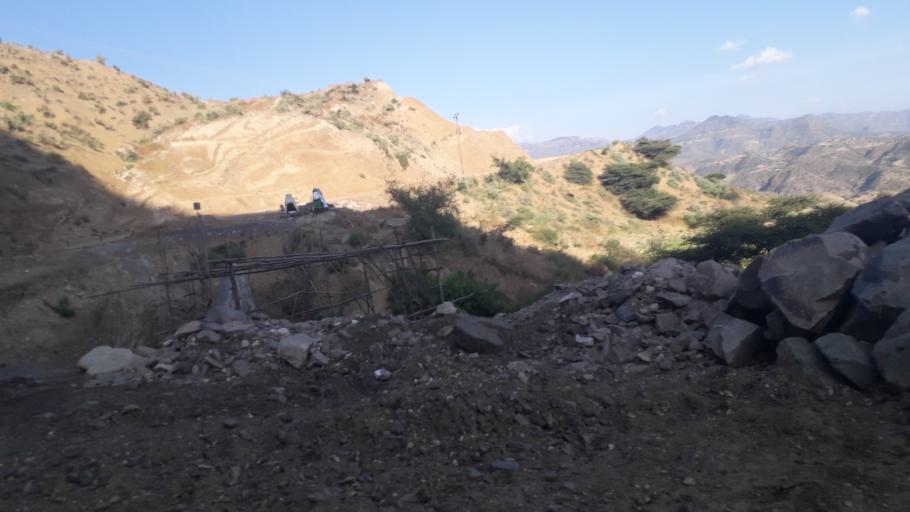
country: ET
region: Amhara
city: Dese
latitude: 11.5175
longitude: 39.2498
